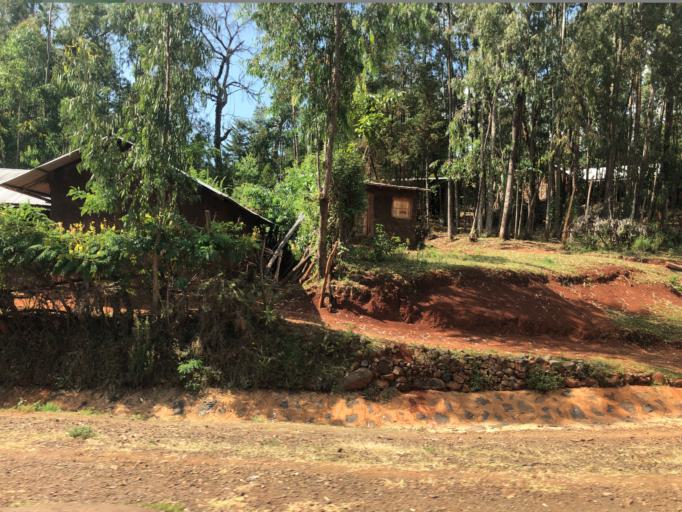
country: ET
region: Southern Nations, Nationalities, and People's Region
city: Gidole
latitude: 5.6440
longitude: 37.3819
